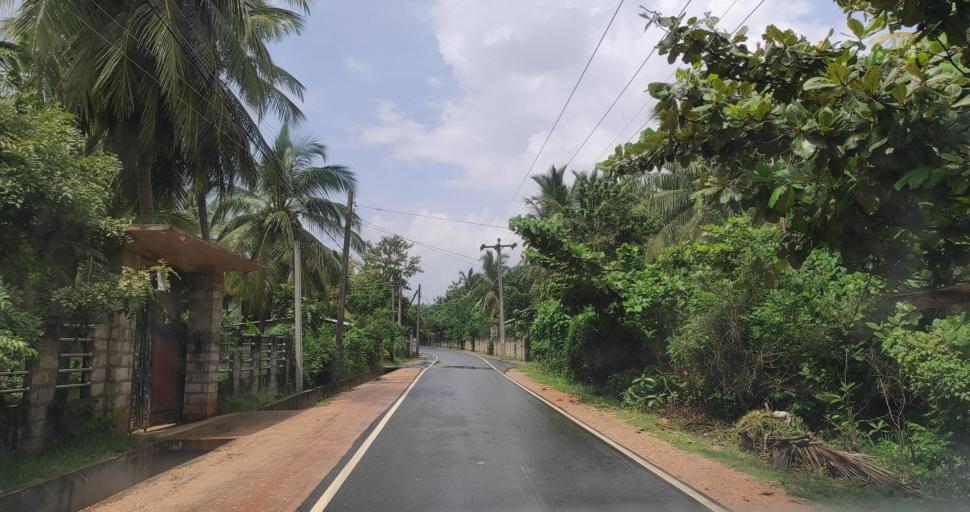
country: LK
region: Eastern Province
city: Trincomalee
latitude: 8.3745
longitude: 81.0086
